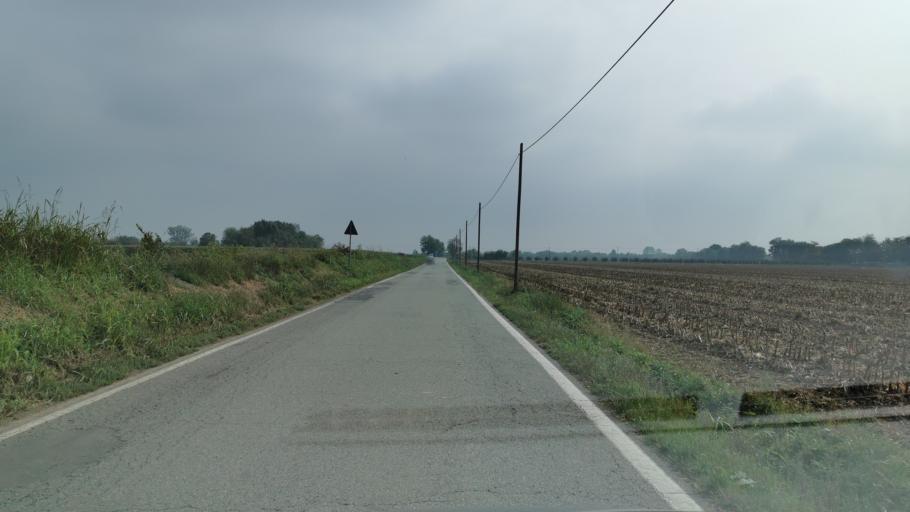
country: IT
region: Piedmont
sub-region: Provincia di Torino
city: Tonengo-Casale
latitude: 45.2656
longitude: 7.9259
